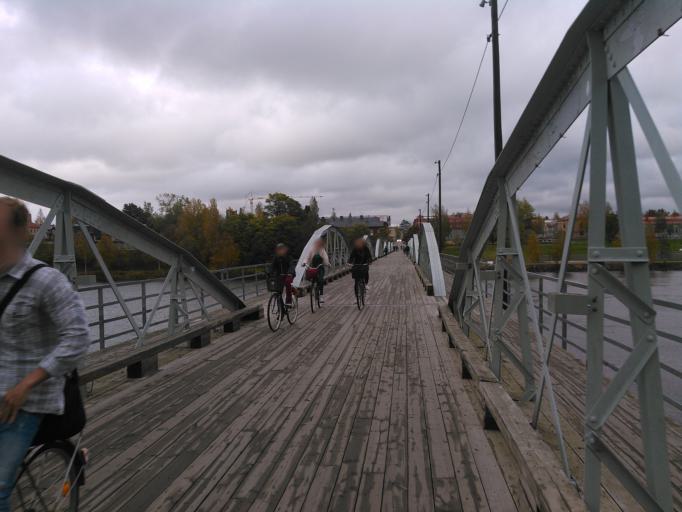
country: SE
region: Vaesterbotten
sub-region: Umea Kommun
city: Umea
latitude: 63.8243
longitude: 20.2487
